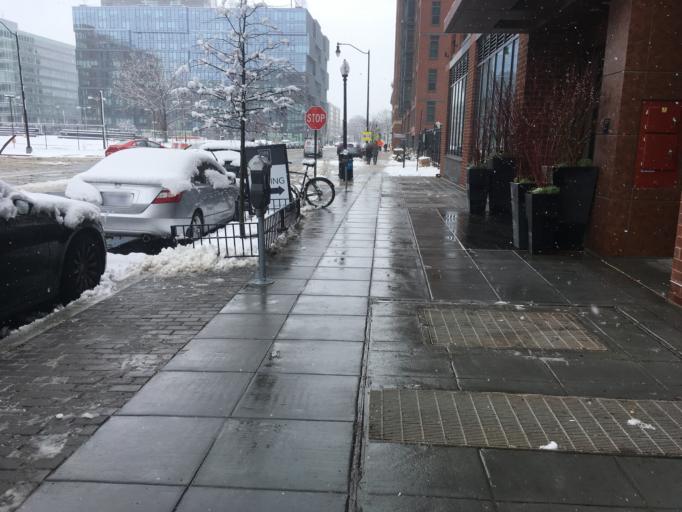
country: US
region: Washington, D.C.
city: Washington, D.C.
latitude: 38.8793
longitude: -77.0055
